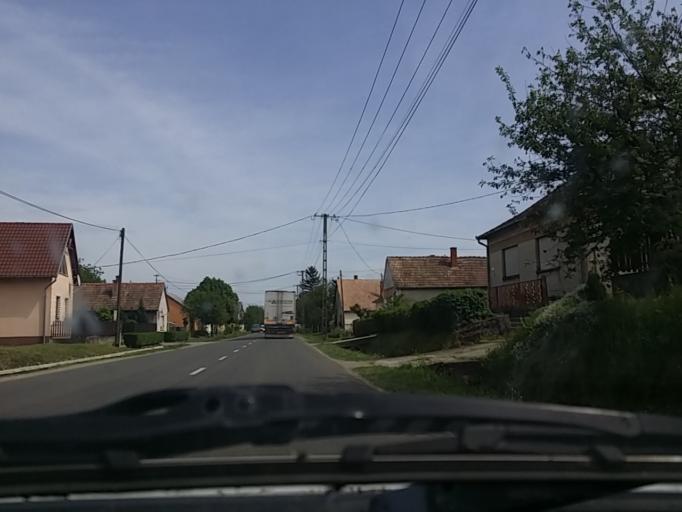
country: HU
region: Baranya
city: Vajszlo
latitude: 45.8625
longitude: 17.9760
